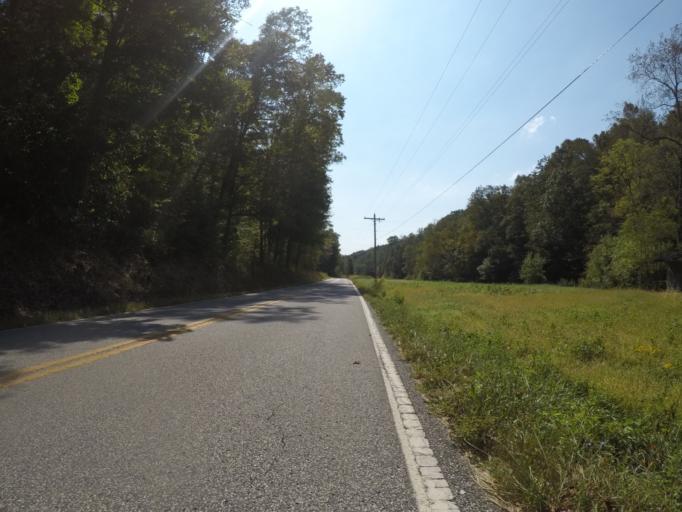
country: US
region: West Virginia
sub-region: Cabell County
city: Lesage
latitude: 38.5732
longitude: -82.4043
